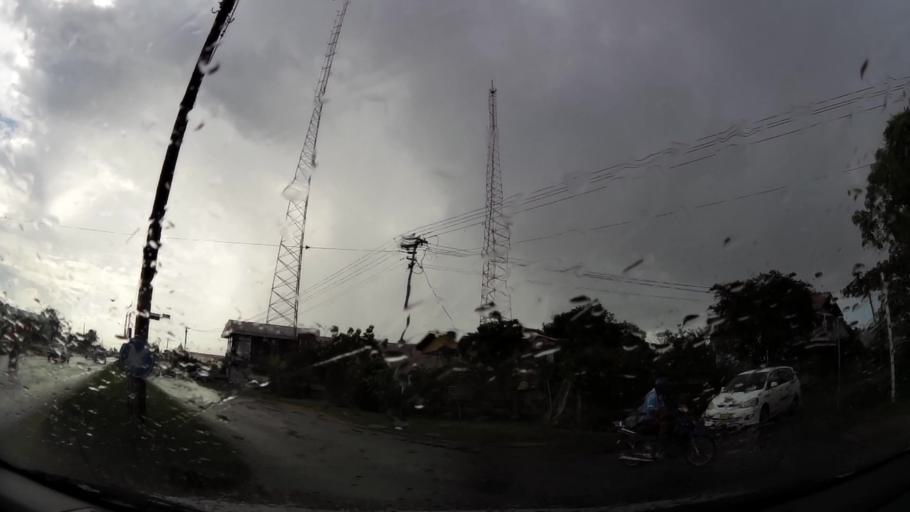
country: SR
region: Paramaribo
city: Paramaribo
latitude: 5.8151
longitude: -55.1894
